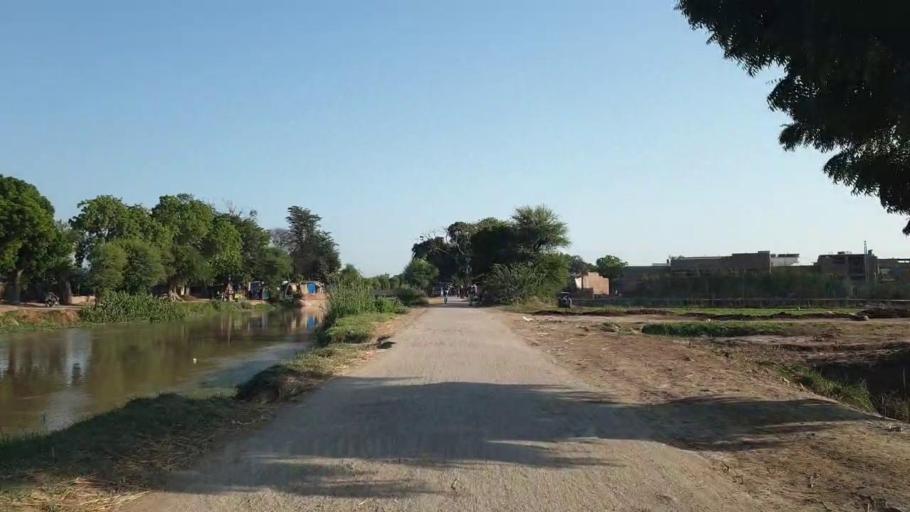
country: PK
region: Sindh
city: Hyderabad
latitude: 25.3172
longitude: 68.4291
